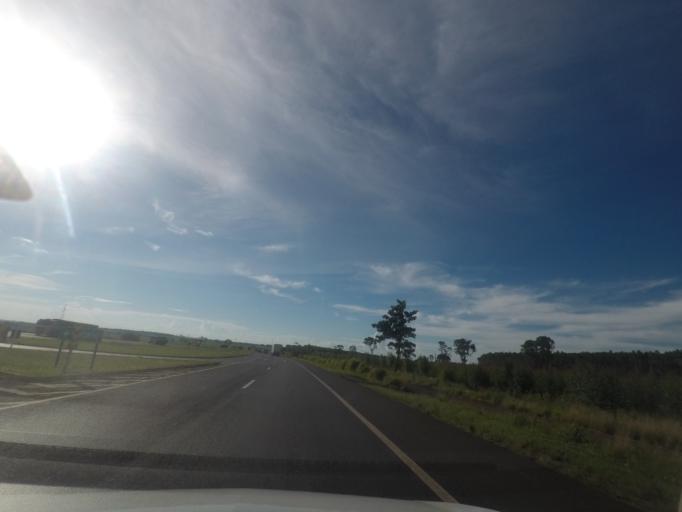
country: BR
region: Minas Gerais
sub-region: Centralina
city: Centralina
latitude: -18.7377
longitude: -49.1006
